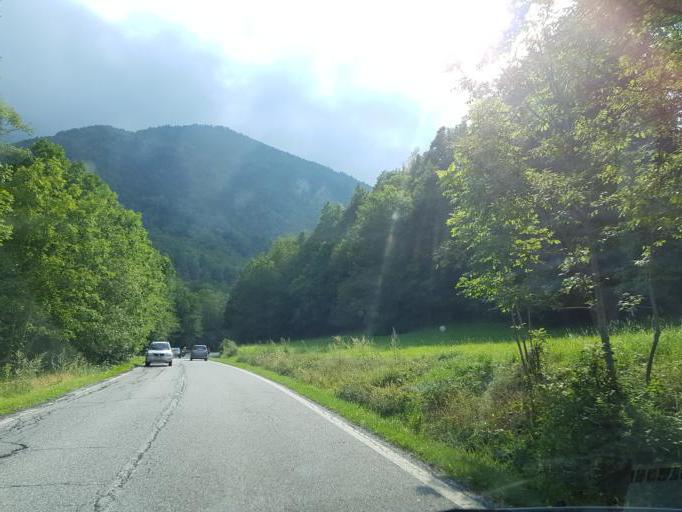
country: IT
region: Piedmont
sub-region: Provincia di Cuneo
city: Sampeyre
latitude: 44.5804
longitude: 7.1643
